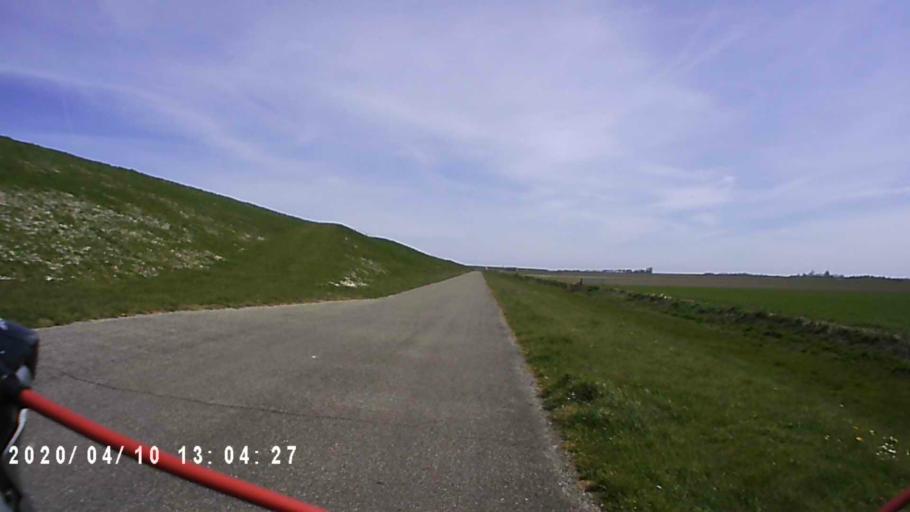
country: NL
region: Groningen
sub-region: Gemeente De Marne
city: Ulrum
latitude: 53.4158
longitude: 6.4042
